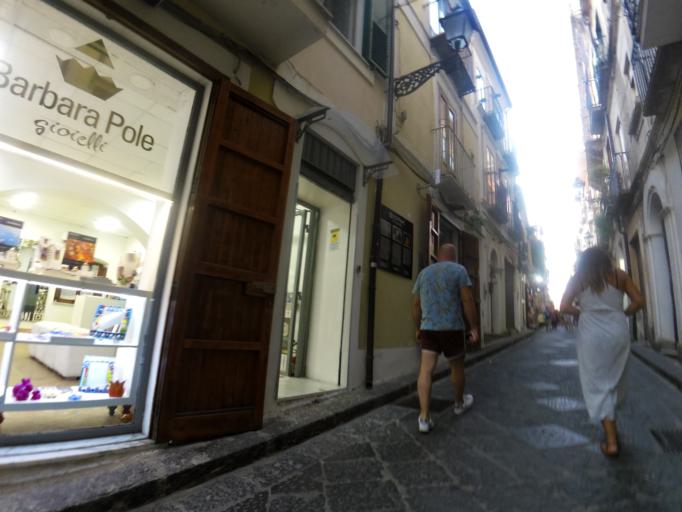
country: IT
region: Calabria
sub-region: Provincia di Vibo-Valentia
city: Maierato
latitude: 38.7359
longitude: 16.1638
